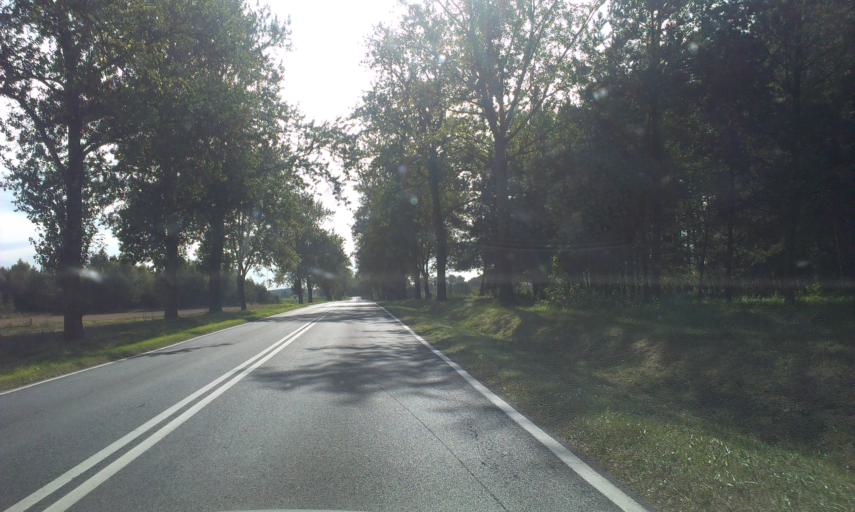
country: PL
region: Greater Poland Voivodeship
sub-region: Powiat zlotowski
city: Okonek
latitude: 53.5750
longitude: 16.8263
